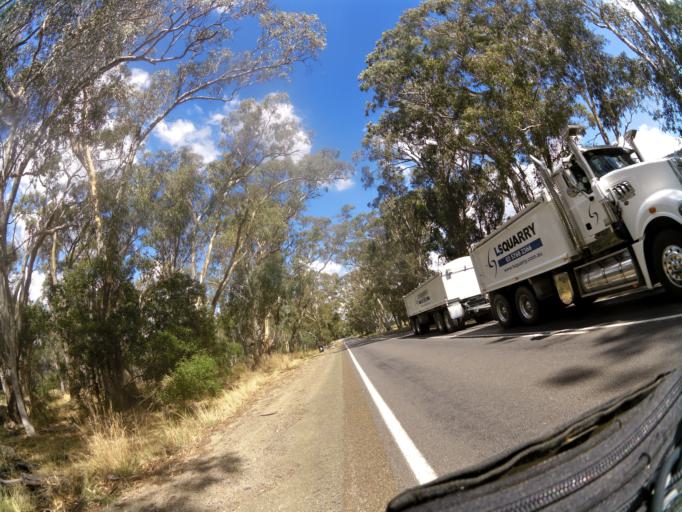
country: AU
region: Victoria
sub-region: Mansfield
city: Mansfield
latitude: -36.8096
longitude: 146.0070
